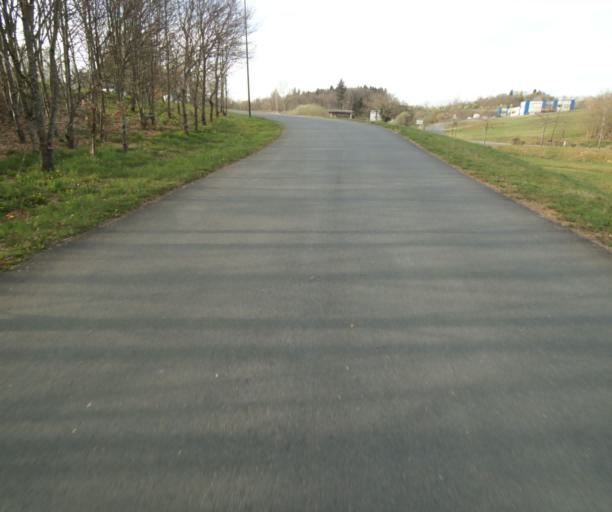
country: FR
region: Limousin
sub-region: Departement de la Correze
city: Naves
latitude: 45.3240
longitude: 1.7656
